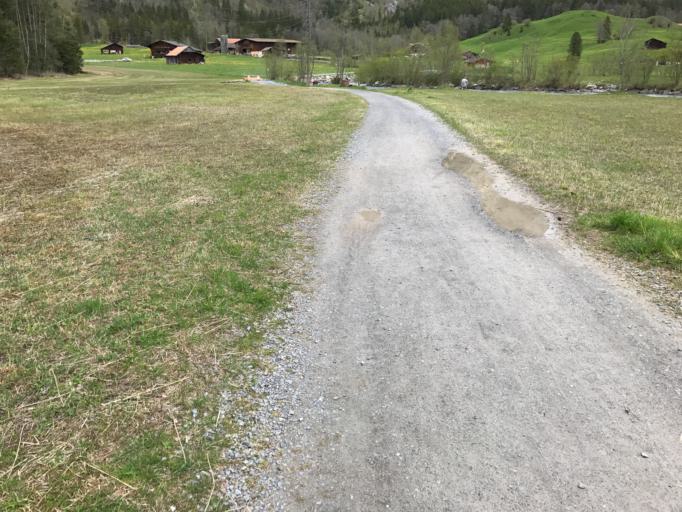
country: CH
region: Bern
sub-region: Frutigen-Niedersimmental District
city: Kandersteg
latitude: 46.4877
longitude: 7.6640
